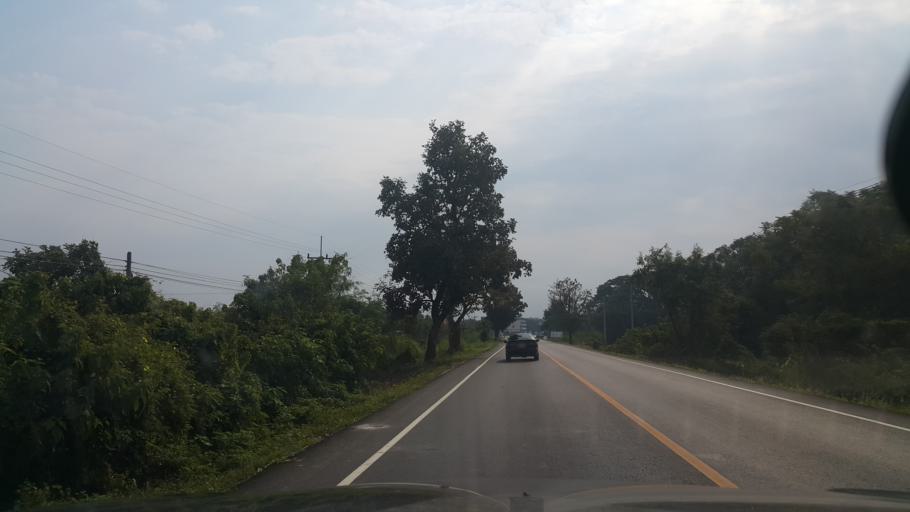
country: TH
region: Sukhothai
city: Si Samrong
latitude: 17.1772
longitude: 99.8471
